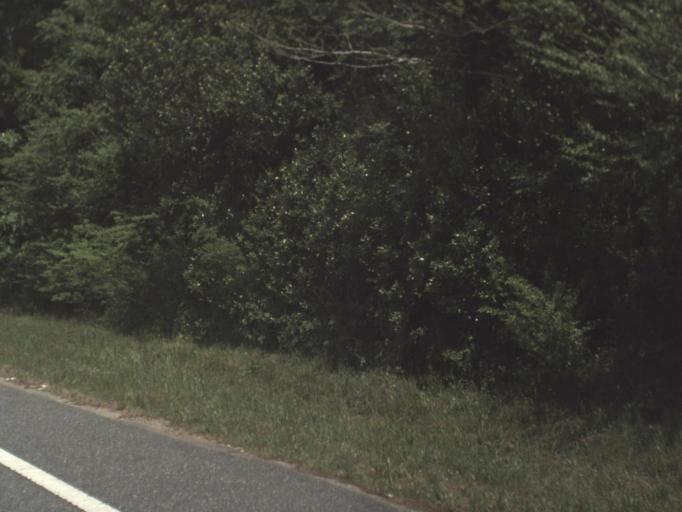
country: US
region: Florida
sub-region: Santa Rosa County
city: Point Baker
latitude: 30.8737
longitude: -87.0524
